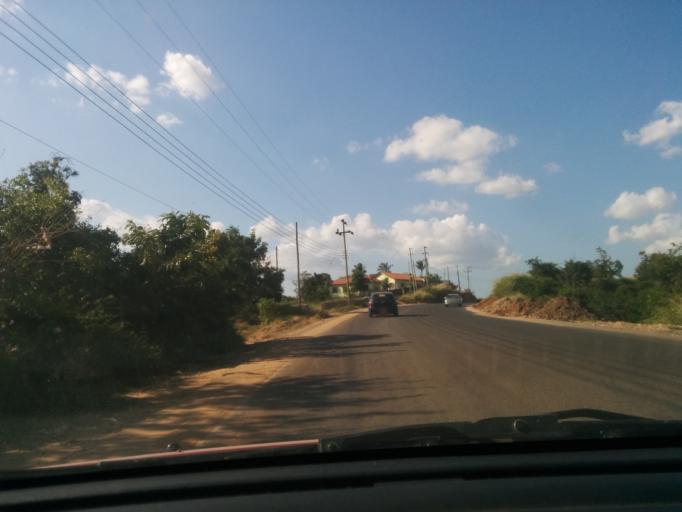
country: TZ
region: Dar es Salaam
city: Magomeni
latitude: -6.7601
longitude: 39.1236
